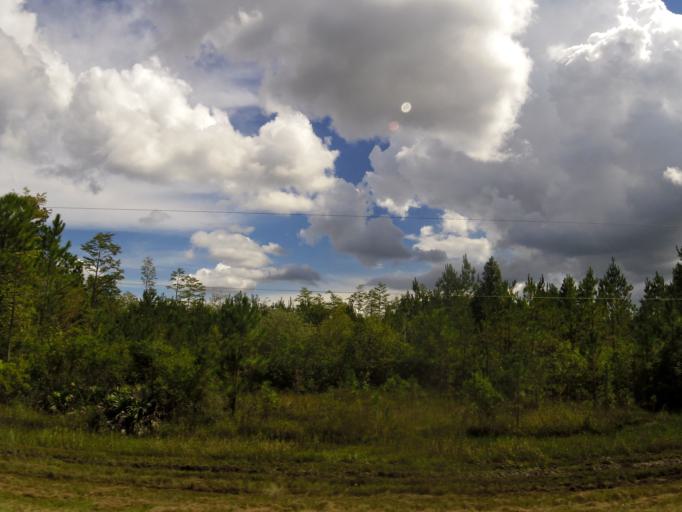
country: US
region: Georgia
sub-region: Brantley County
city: Nahunta
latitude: 31.0478
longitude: -82.0179
